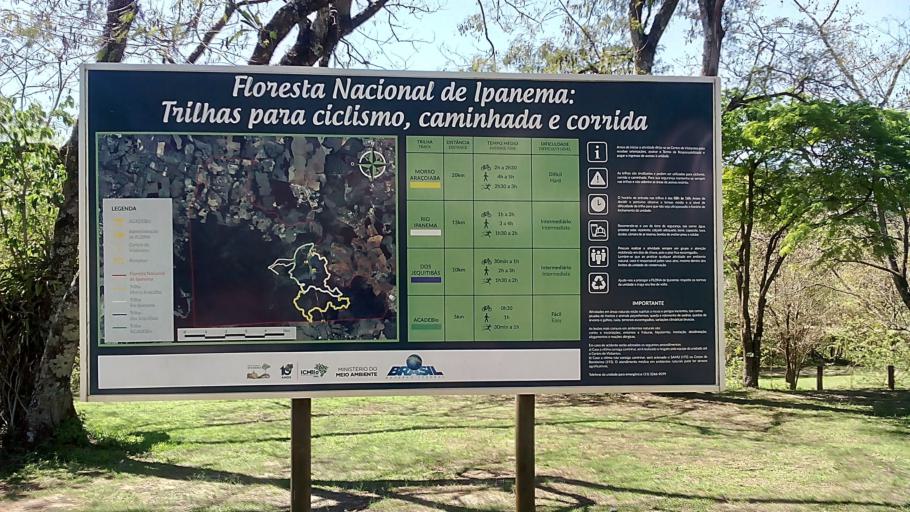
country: BR
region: Sao Paulo
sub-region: Aracoiaba Da Serra
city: Aracoiaba da Serra
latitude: -23.4252
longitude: -47.5975
